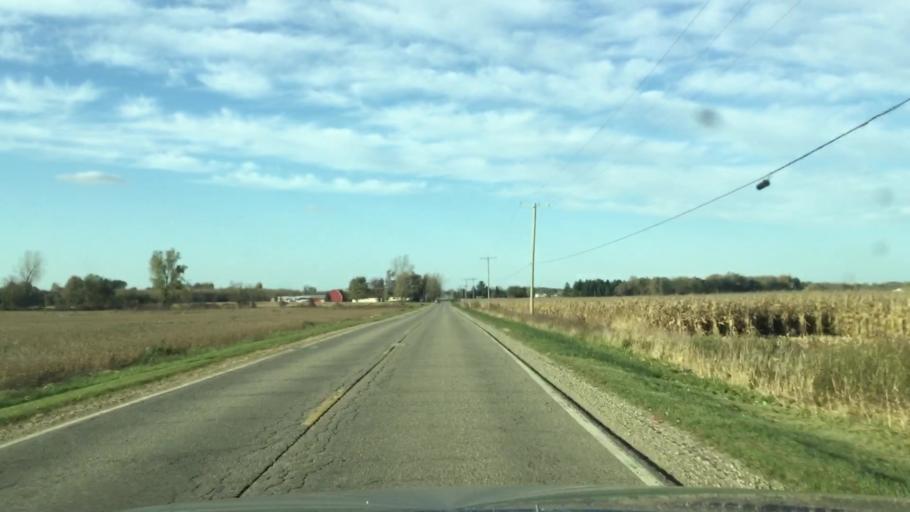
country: US
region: Michigan
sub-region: Lapeer County
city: North Branch
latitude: 43.2823
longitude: -83.1984
